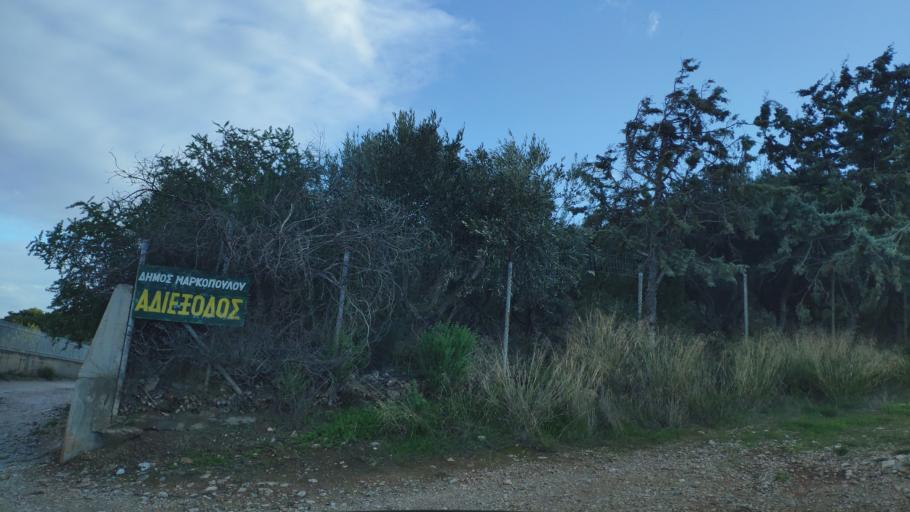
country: GR
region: Attica
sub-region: Nomarchia Anatolikis Attikis
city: Limin Mesoyaias
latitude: 37.9242
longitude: 24.0067
